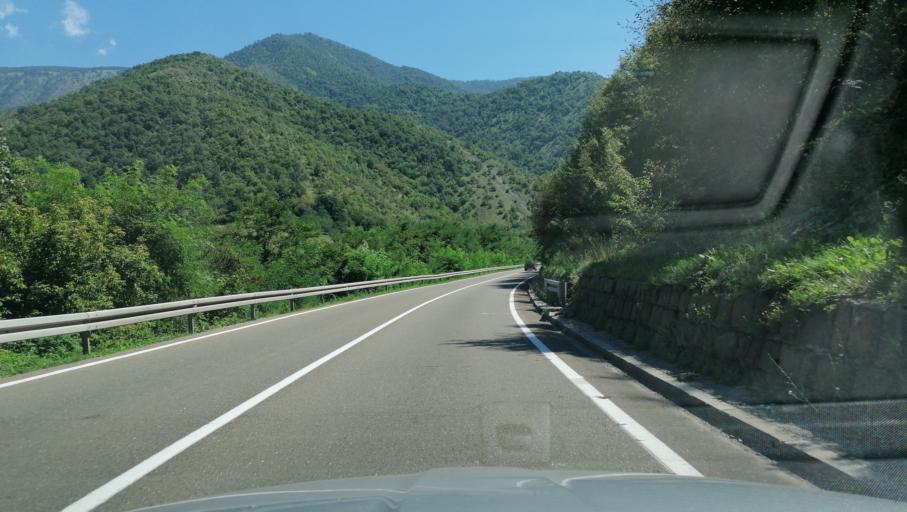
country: RS
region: Central Serbia
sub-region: Raski Okrug
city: Kraljevo
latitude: 43.5956
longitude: 20.5670
